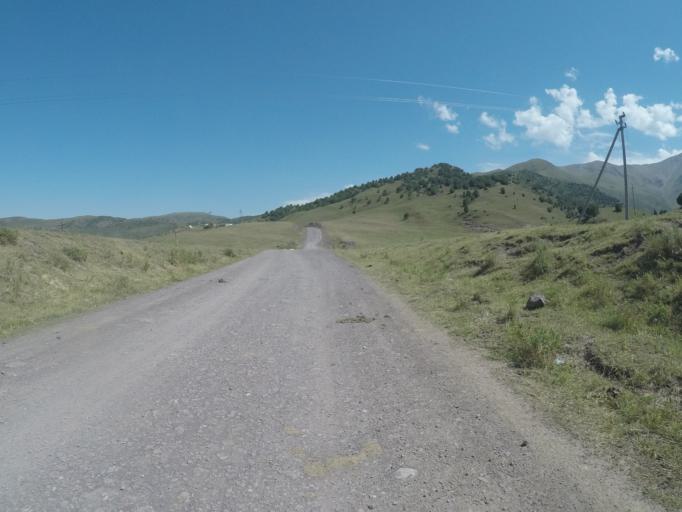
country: KG
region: Chuy
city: Bishkek
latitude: 42.6502
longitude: 74.5301
